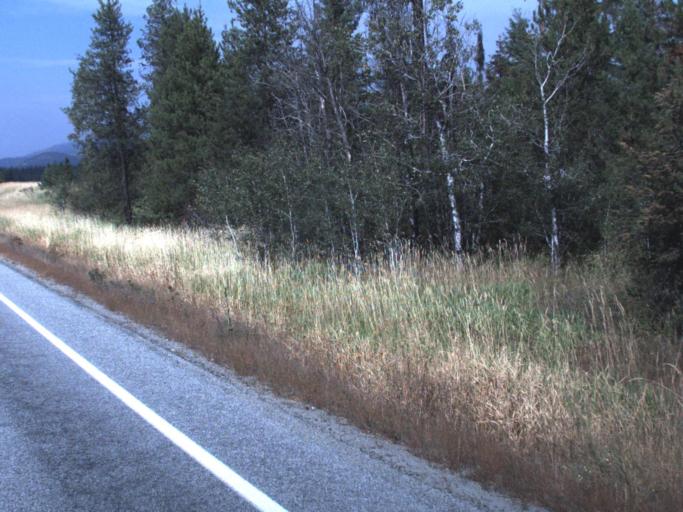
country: US
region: Washington
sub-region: Pend Oreille County
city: Newport
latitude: 48.2842
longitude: -117.2846
